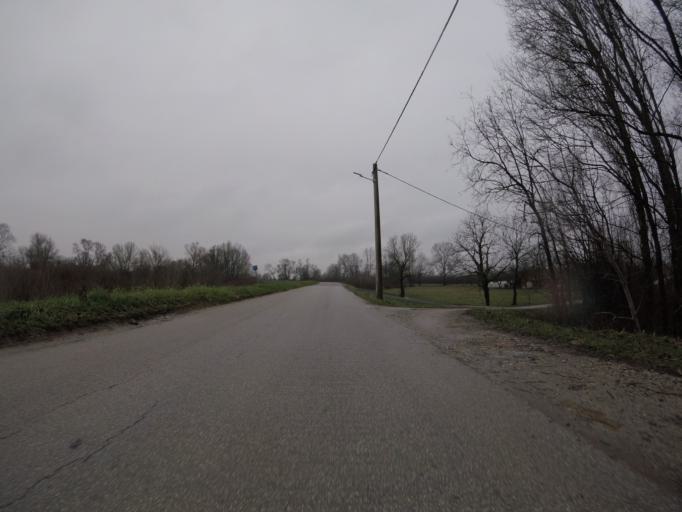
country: HR
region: Sisacko-Moslavacka
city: Lekenik
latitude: 45.6694
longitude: 16.2444
